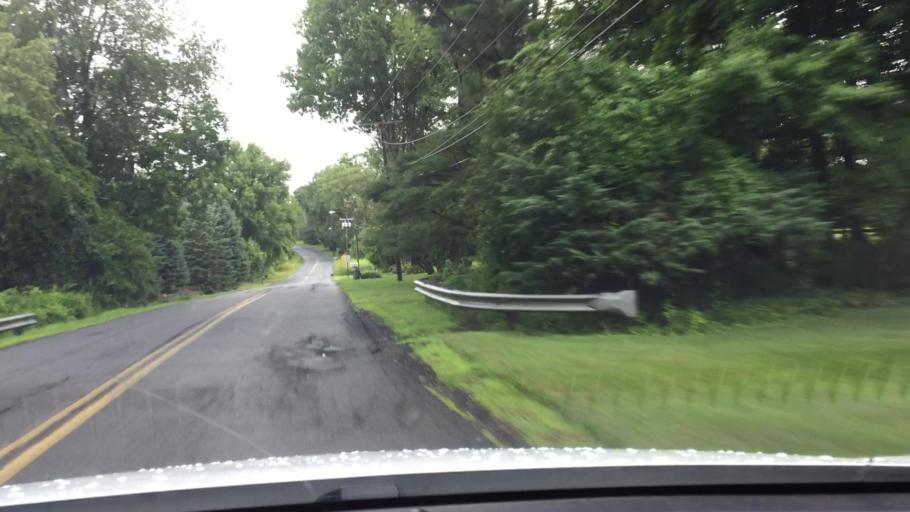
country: US
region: Massachusetts
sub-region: Berkshire County
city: Dalton
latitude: 42.4253
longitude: -73.1936
